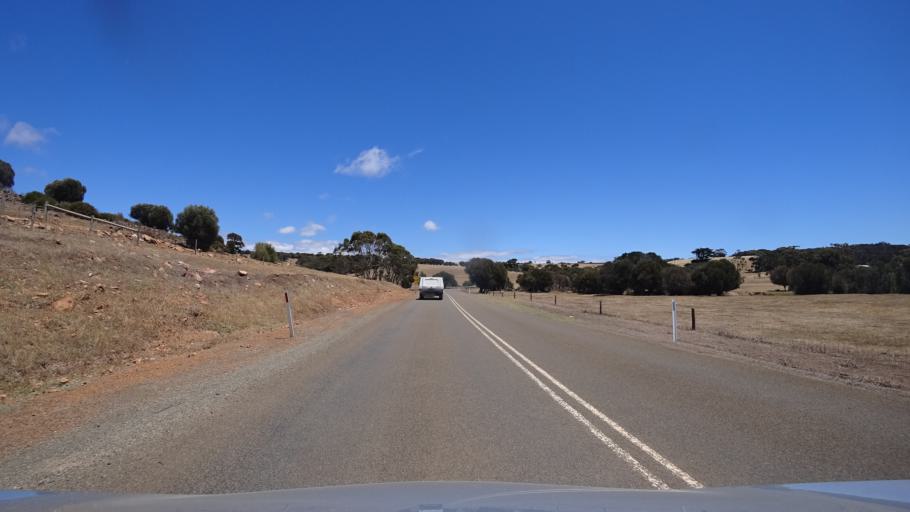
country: AU
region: South Australia
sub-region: Kangaroo Island
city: Kingscote
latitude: -35.6280
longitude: 137.2061
